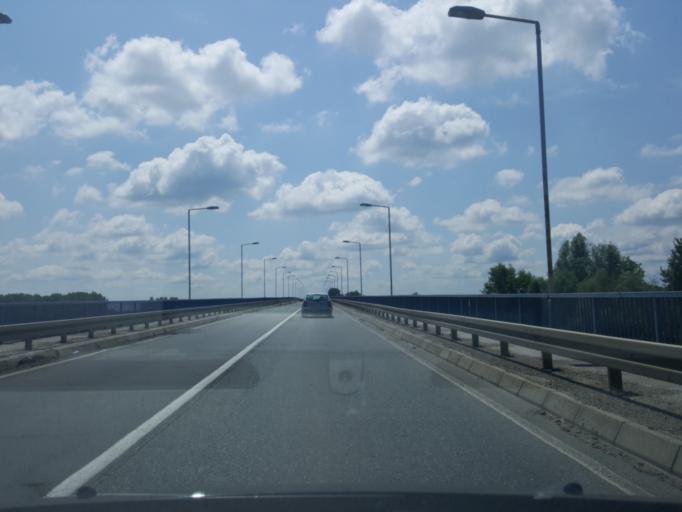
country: RS
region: Autonomna Pokrajina Vojvodina
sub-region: Sremski Okrug
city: Sremska Mitrovica
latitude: 44.9621
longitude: 19.6311
